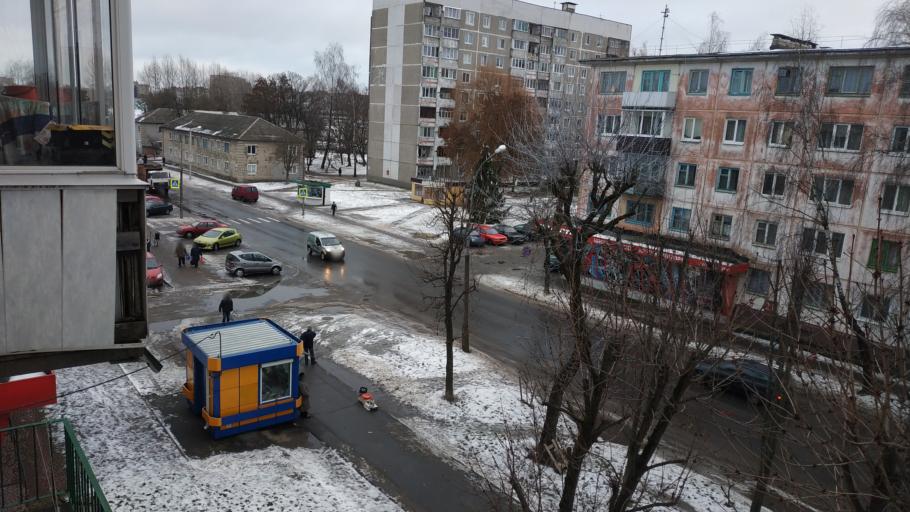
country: BY
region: Mogilev
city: Mahilyow
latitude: 53.9079
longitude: 30.2968
